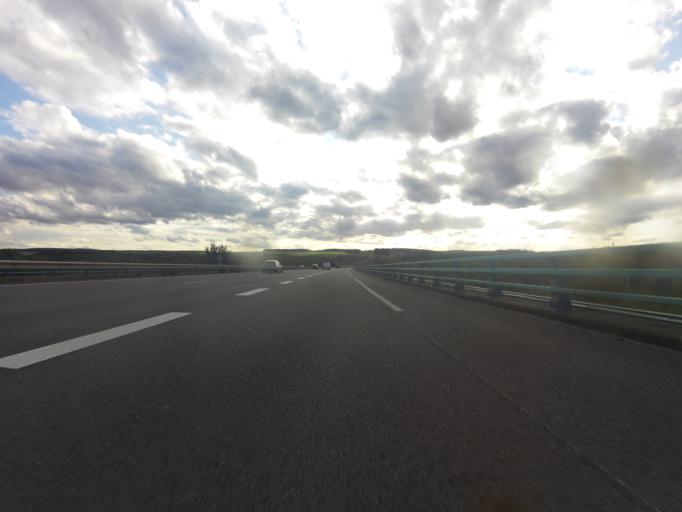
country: FR
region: Picardie
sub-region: Departement de la Somme
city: Longueau
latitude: 49.8617
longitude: 2.3706
